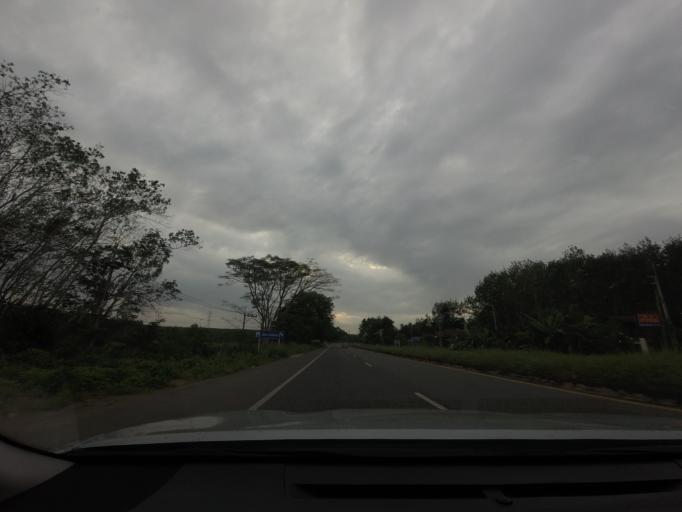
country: TH
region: Surat Thani
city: Phunphin
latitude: 9.0371
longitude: 99.1394
